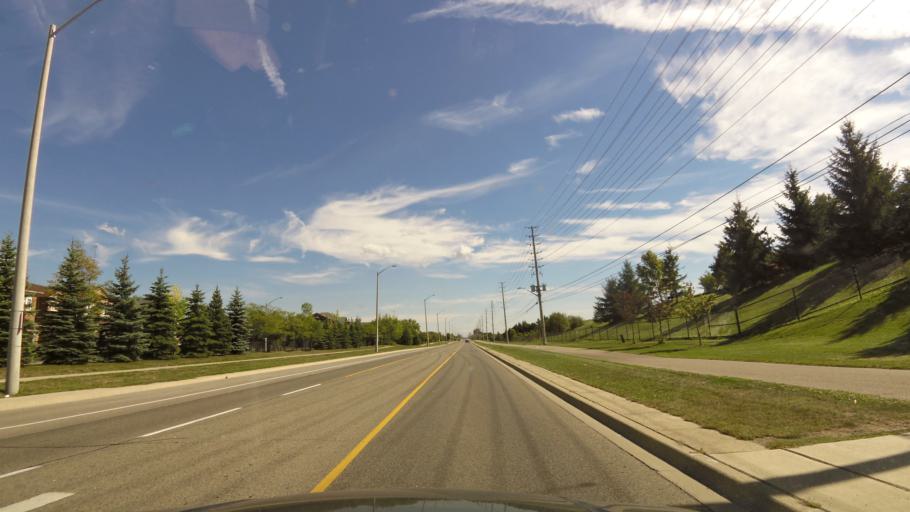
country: CA
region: Ontario
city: Mississauga
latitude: 43.6027
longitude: -79.6951
